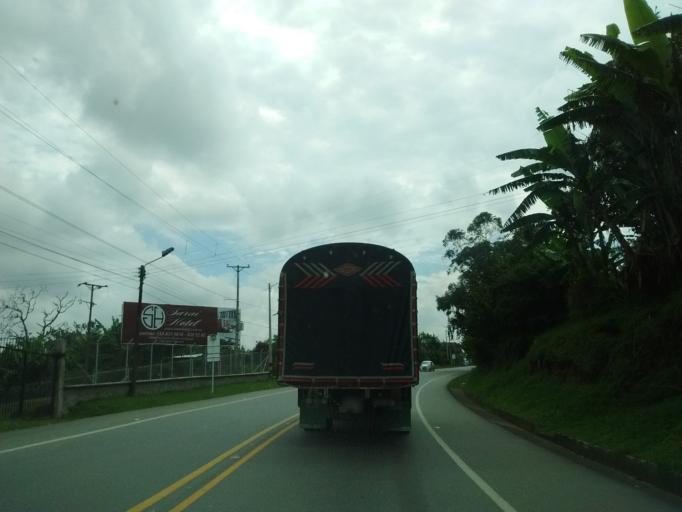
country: CO
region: Cauca
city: Cajibio
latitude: 2.5254
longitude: -76.5509
